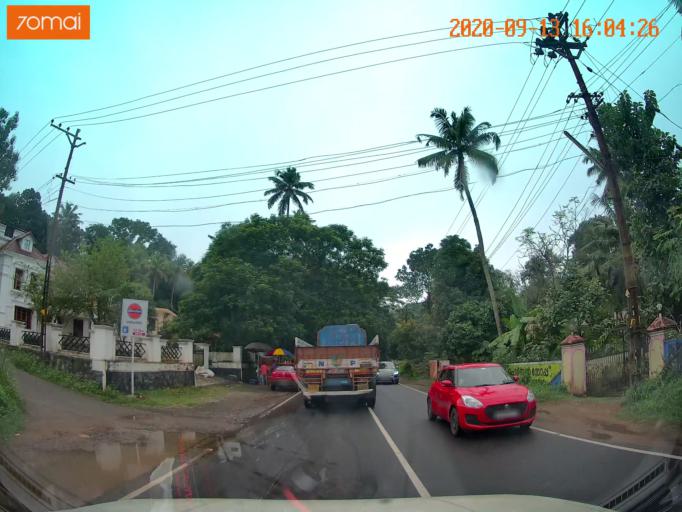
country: IN
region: Kerala
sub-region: Kottayam
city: Palackattumala
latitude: 9.6717
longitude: 76.5703
